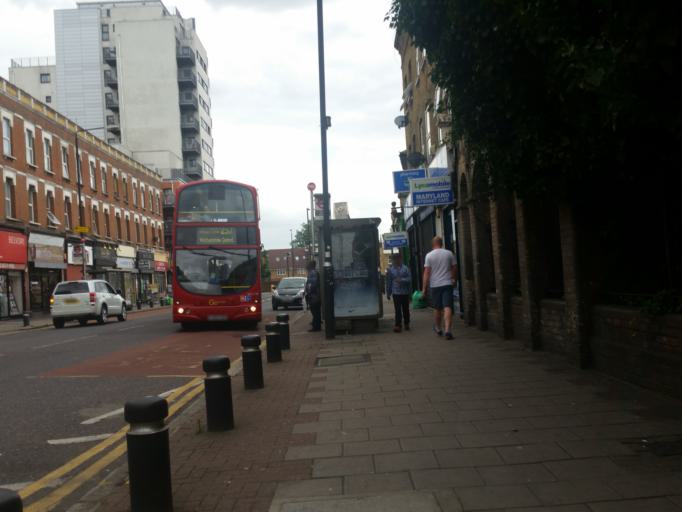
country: GB
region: England
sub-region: Greater London
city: Poplar
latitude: 51.5473
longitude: 0.0060
